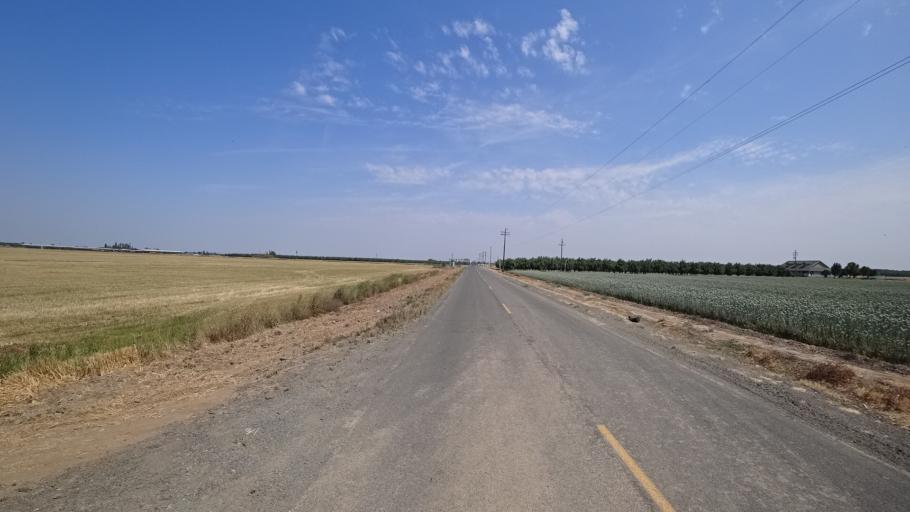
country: US
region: California
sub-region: Kings County
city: Armona
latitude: 36.3320
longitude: -119.7448
